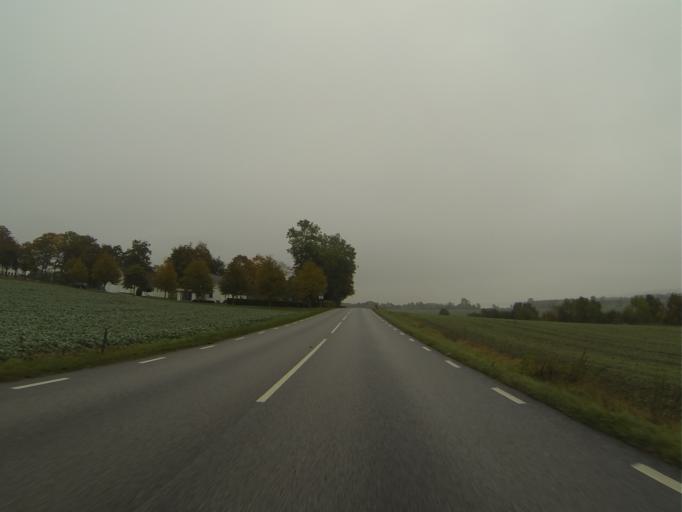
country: SE
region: Skane
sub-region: Hoors Kommun
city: Loberod
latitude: 55.7110
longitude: 13.5465
